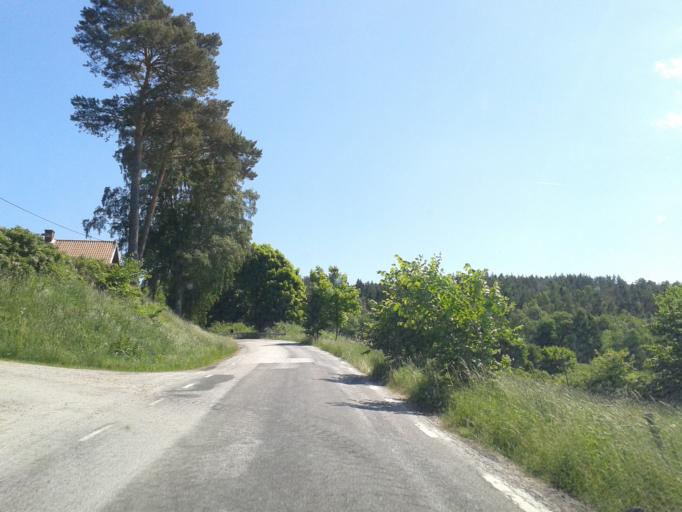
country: SE
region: Vaestra Goetaland
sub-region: Stenungsunds Kommun
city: Stora Hoga
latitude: 58.0199
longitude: 11.8844
